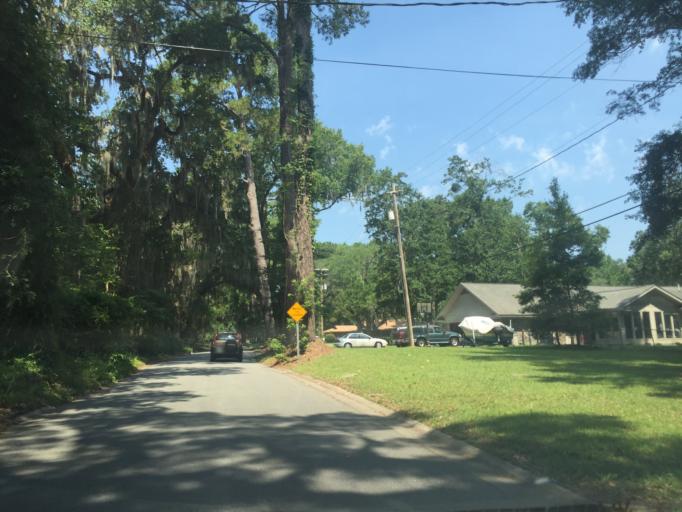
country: US
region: Georgia
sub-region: Chatham County
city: Montgomery
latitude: 31.9718
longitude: -81.1295
